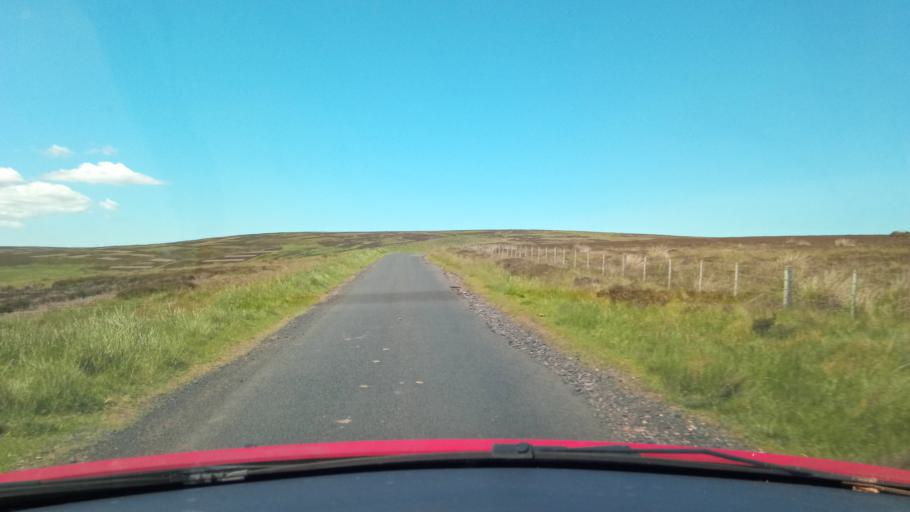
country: GB
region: Scotland
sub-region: East Lothian
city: Dunbar
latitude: 55.8292
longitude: -2.5258
